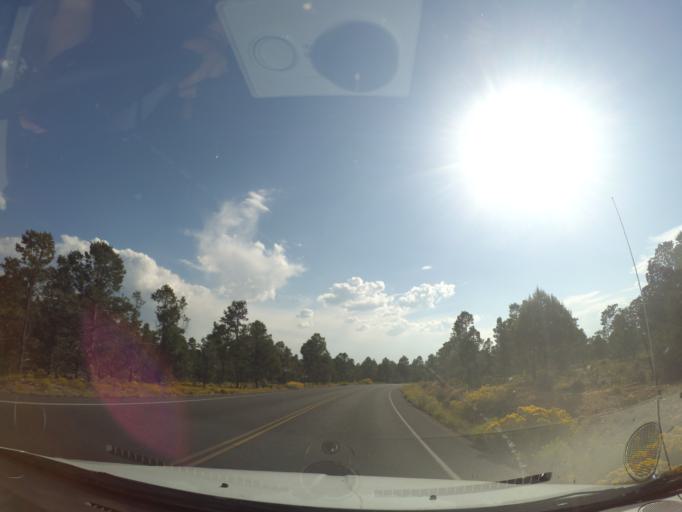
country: US
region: Arizona
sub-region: Coconino County
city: Grand Canyon
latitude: 36.0579
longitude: -112.1132
